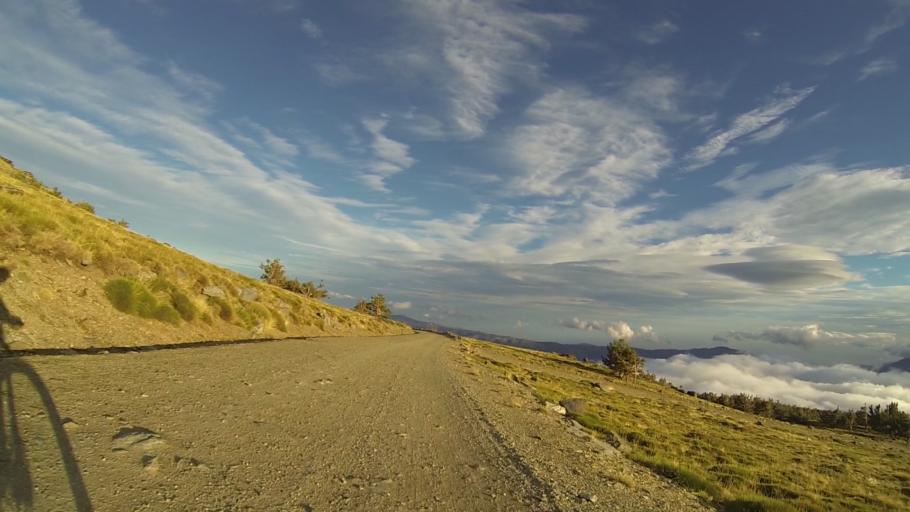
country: ES
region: Andalusia
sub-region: Provincia de Granada
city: Capileira
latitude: 36.9791
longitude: -3.3298
